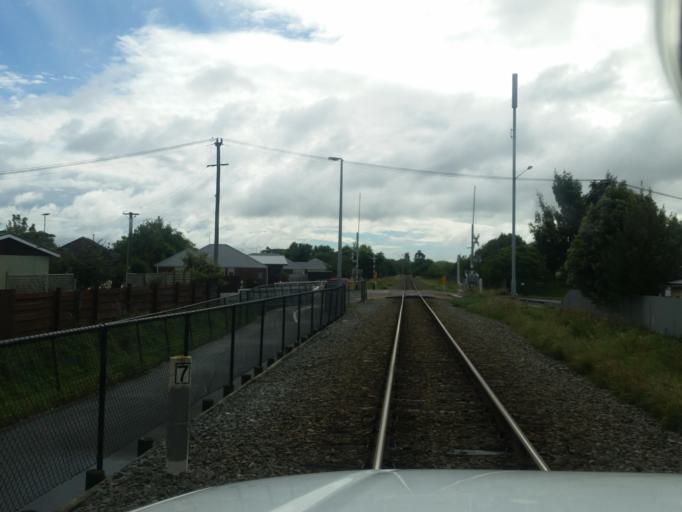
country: NZ
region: Canterbury
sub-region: Christchurch City
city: Christchurch
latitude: -43.4803
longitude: 172.6088
